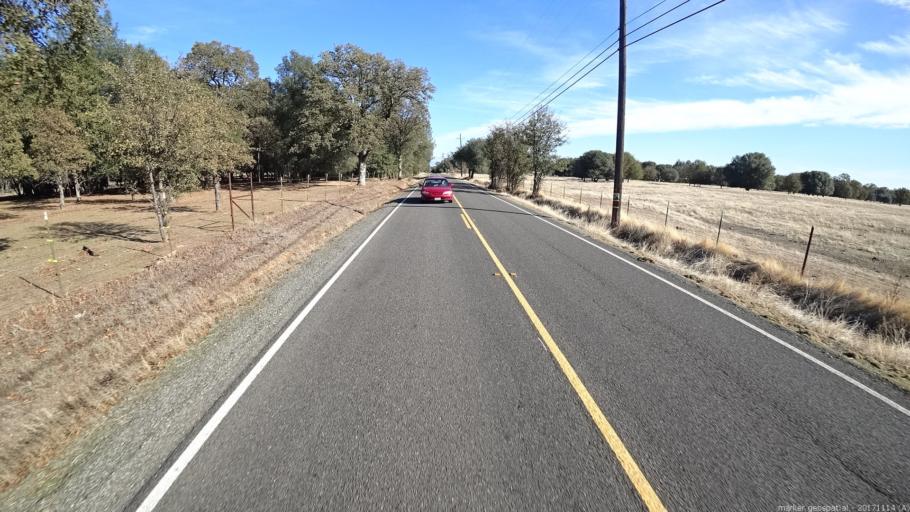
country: US
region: California
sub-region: Shasta County
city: Anderson
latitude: 40.3884
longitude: -122.4304
